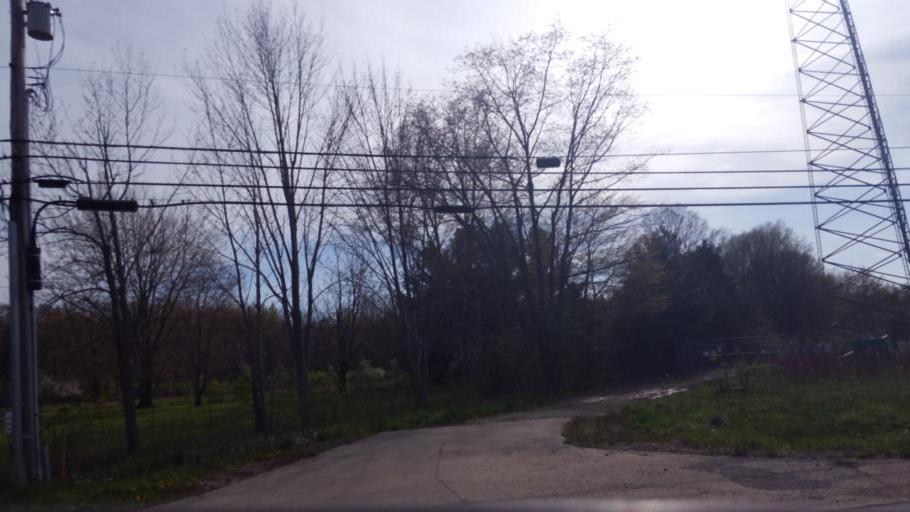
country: US
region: Ohio
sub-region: Ashtabula County
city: Geneva-on-the-Lake
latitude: 41.8396
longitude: -80.9548
